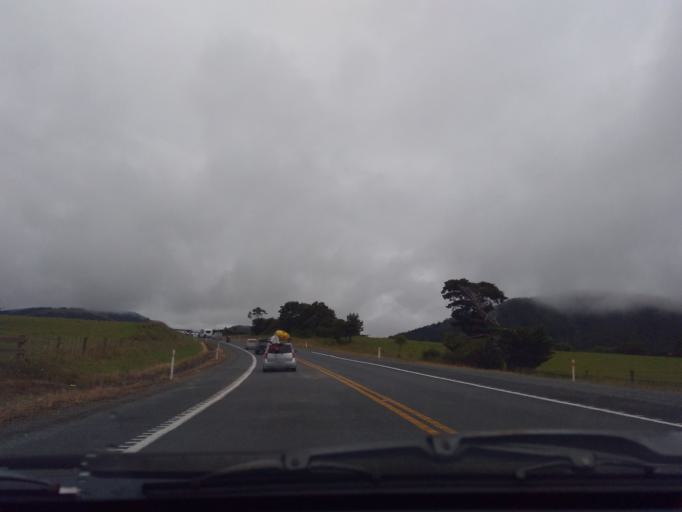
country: NZ
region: Auckland
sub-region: Auckland
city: Wellsford
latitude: -36.1459
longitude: 174.4379
